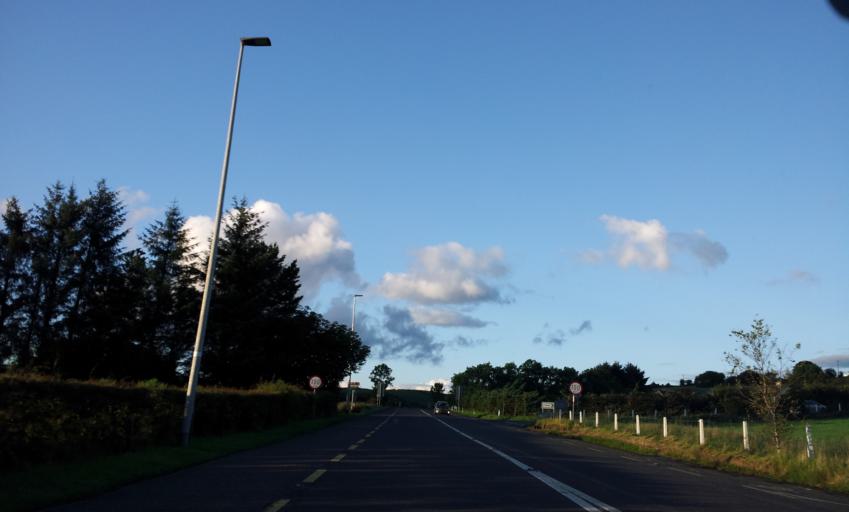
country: IE
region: Munster
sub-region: County Limerick
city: Newcastle West
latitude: 52.4008
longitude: -9.1712
